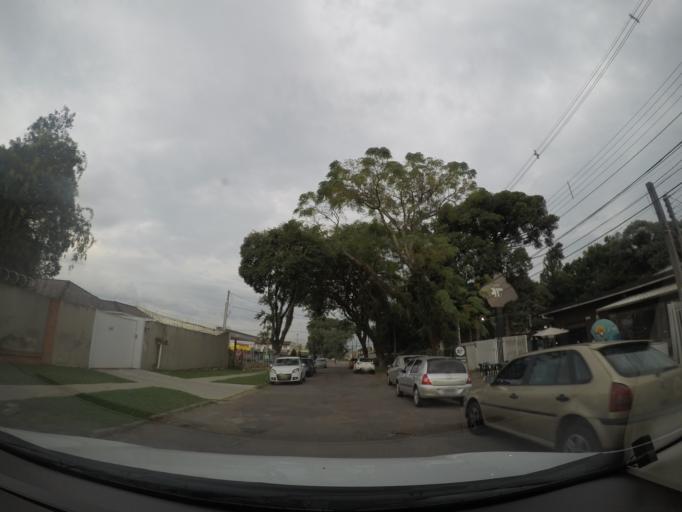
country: BR
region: Parana
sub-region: Sao Jose Dos Pinhais
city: Sao Jose dos Pinhais
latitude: -25.5193
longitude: -49.2357
